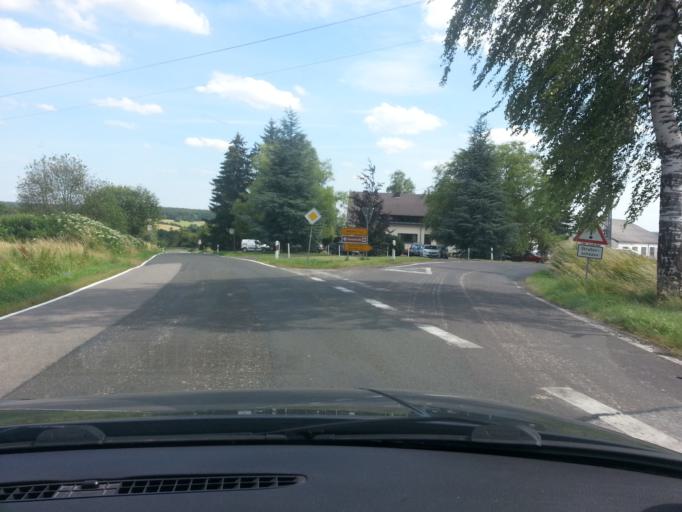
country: DE
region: Rheinland-Pfalz
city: Hornbach
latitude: 49.1754
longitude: 7.3020
